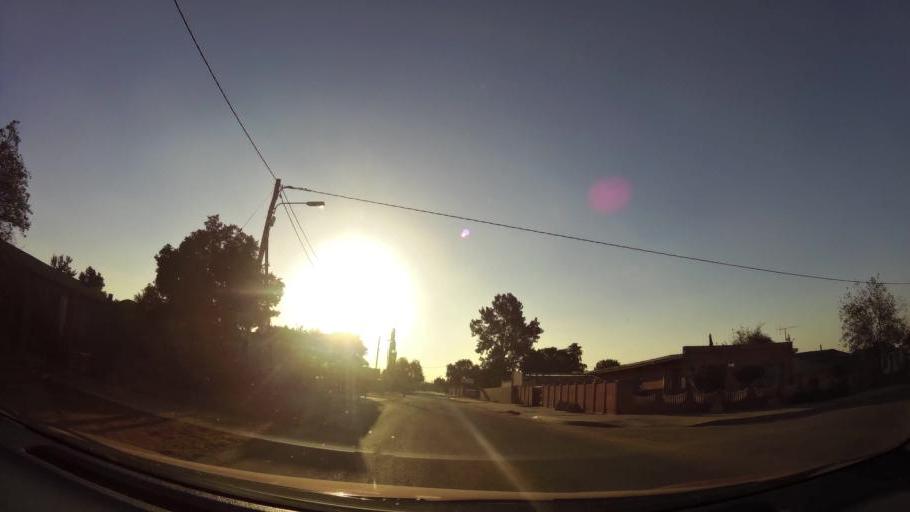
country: ZA
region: North-West
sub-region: Bojanala Platinum District Municipality
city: Rustenburg
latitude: -25.6336
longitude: 27.2139
